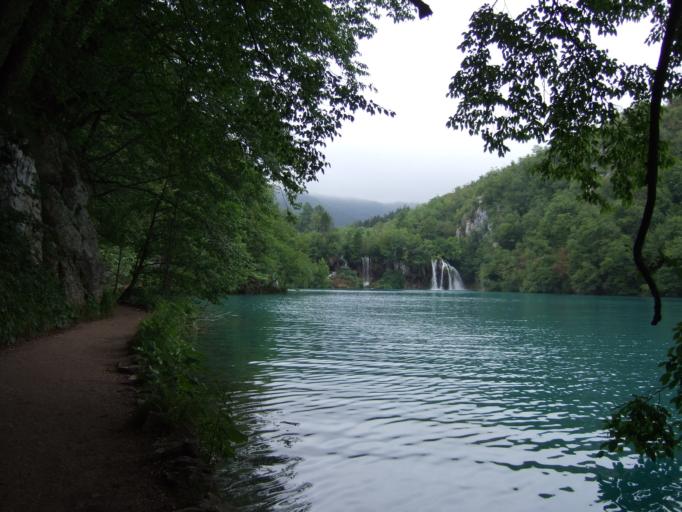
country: HR
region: Licko-Senjska
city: Jezerce
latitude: 44.8958
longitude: 15.6114
